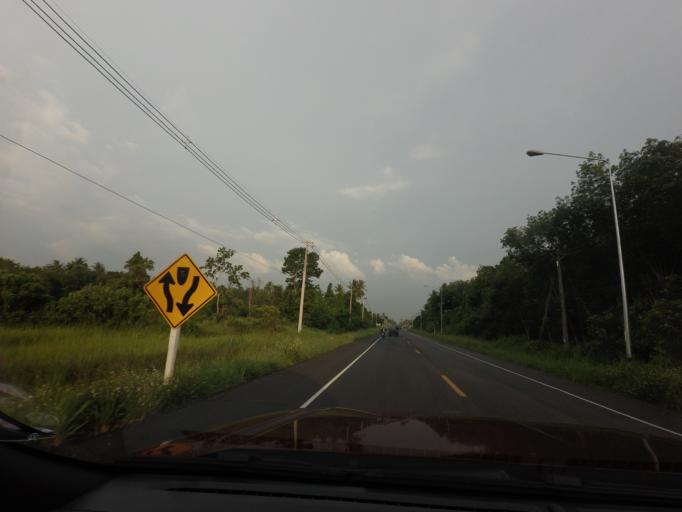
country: TH
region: Pattani
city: Mae Lan
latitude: 6.6547
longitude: 101.1738
